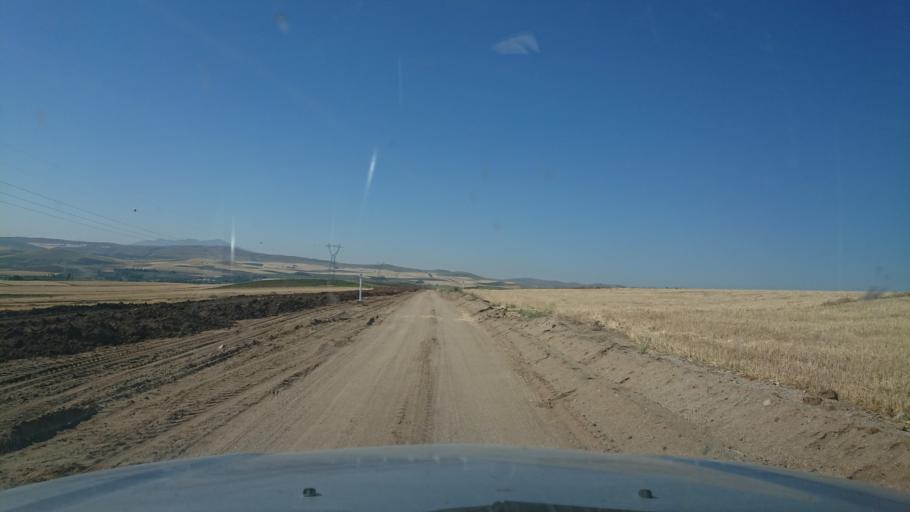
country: TR
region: Aksaray
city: Agacoren
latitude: 38.8408
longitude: 33.9442
